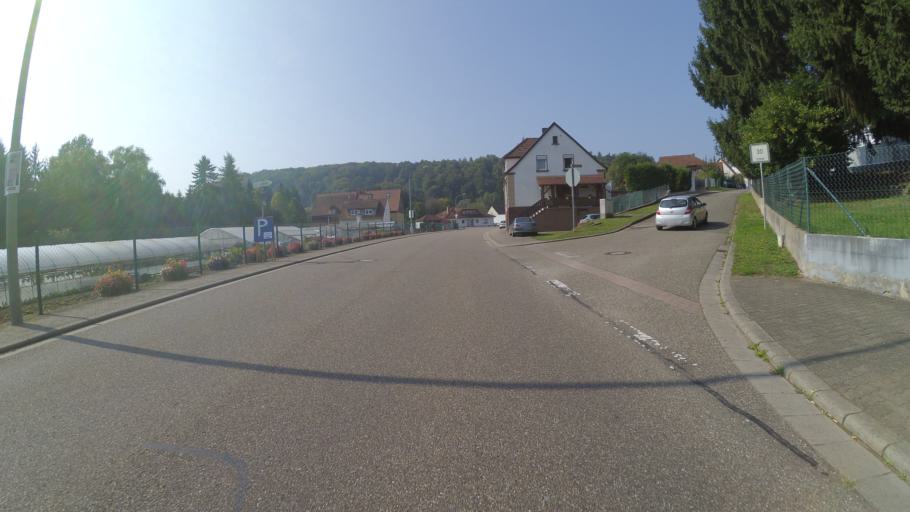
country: DE
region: Rheinland-Pfalz
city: Dellfeld
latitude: 49.2296
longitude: 7.4675
